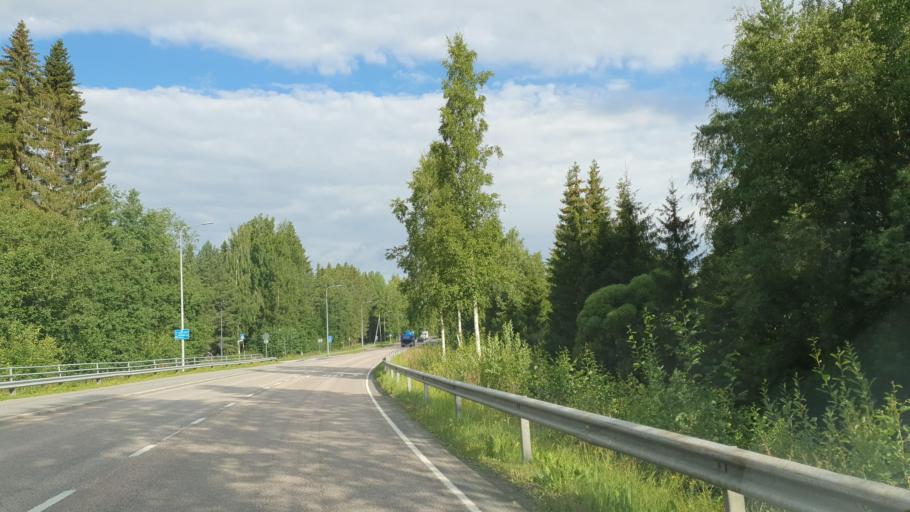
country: FI
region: Central Finland
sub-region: Jyvaeskylae
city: Jyvaeskylae
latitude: 62.1816
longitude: 25.7241
